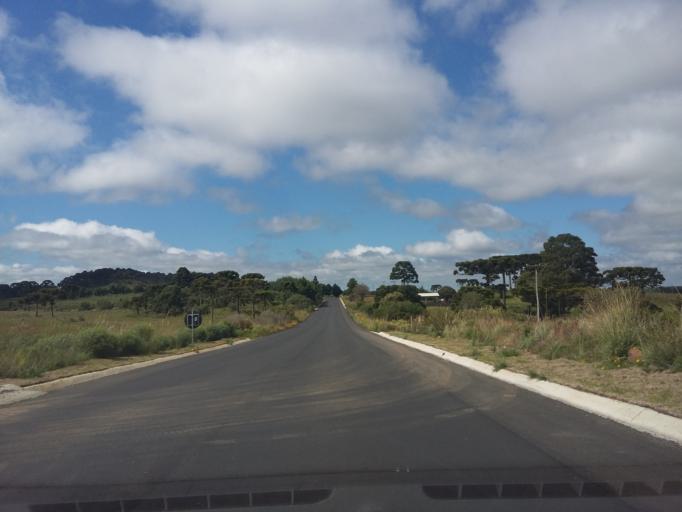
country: BR
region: Santa Catarina
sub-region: Sao Joaquim
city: Sao Joaquim
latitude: -28.0363
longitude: -50.0747
